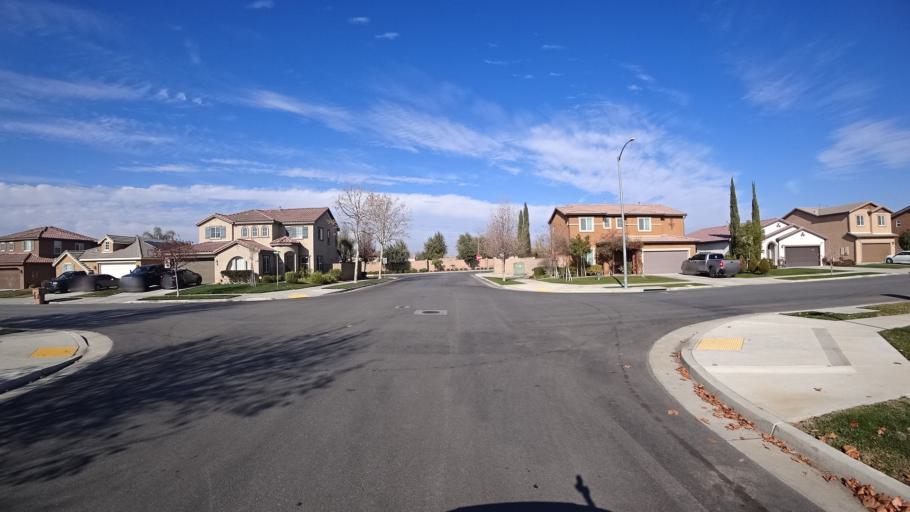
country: US
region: California
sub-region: Kern County
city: Oildale
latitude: 35.4075
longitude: -118.8901
